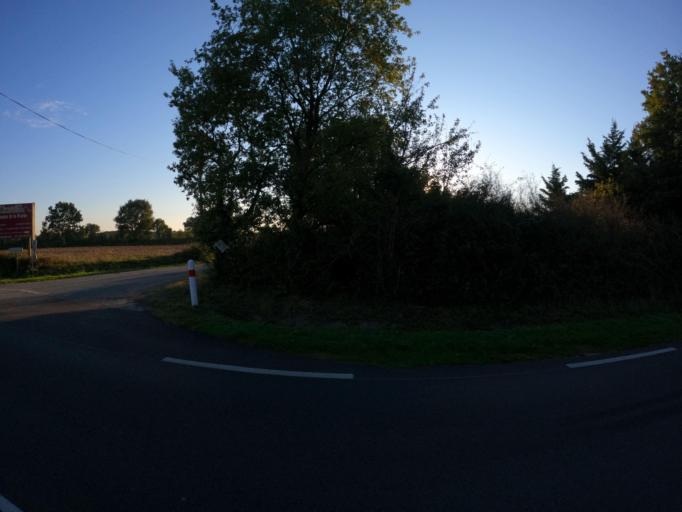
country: FR
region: Pays de la Loire
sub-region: Departement de la Vendee
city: Bournezeau
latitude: 46.6218
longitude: -1.1558
